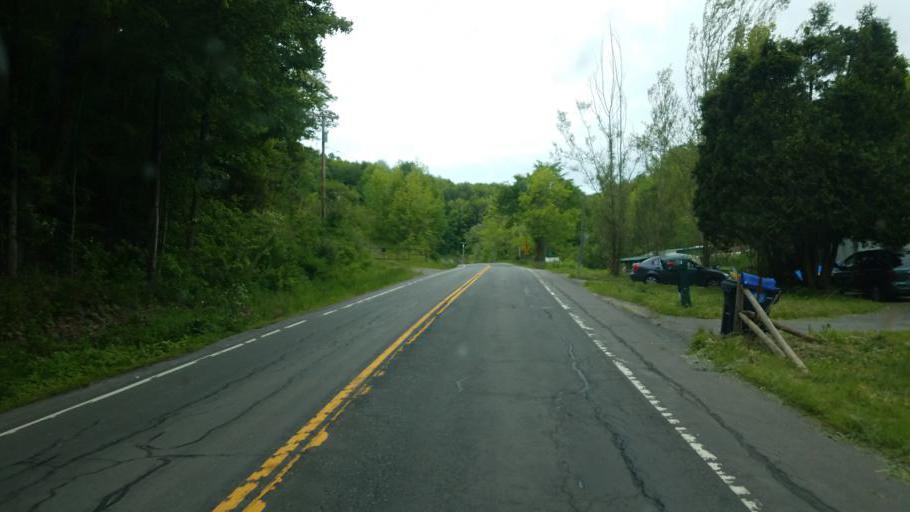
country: US
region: New York
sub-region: Herkimer County
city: Frankfort
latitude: 42.9678
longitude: -75.1009
